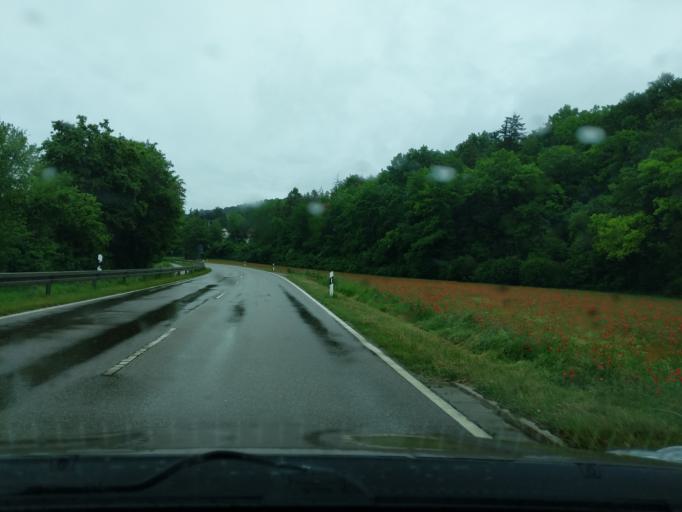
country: DE
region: Bavaria
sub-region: Upper Palatinate
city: Sinzing
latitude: 49.0334
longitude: 12.0321
